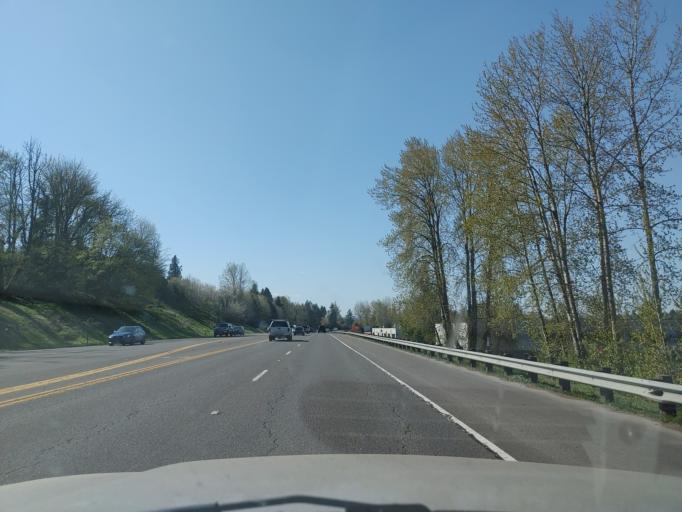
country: US
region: Oregon
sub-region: Clackamas County
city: Milwaukie
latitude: 45.4351
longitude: -122.6179
